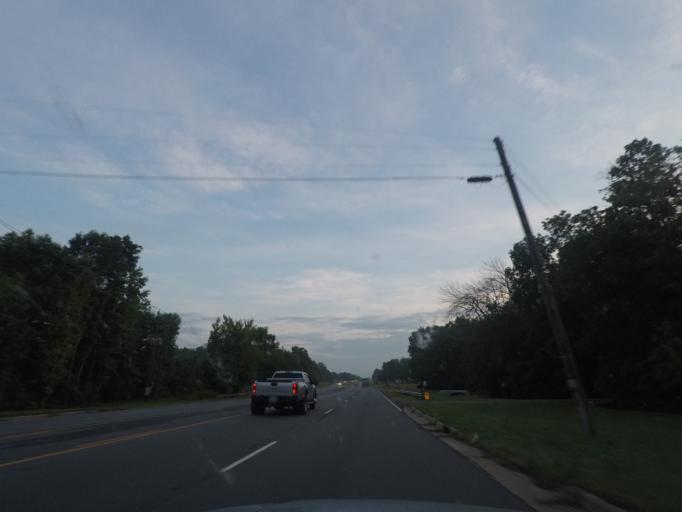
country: US
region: North Carolina
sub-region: Person County
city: Roxboro
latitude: 36.2232
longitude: -78.9283
